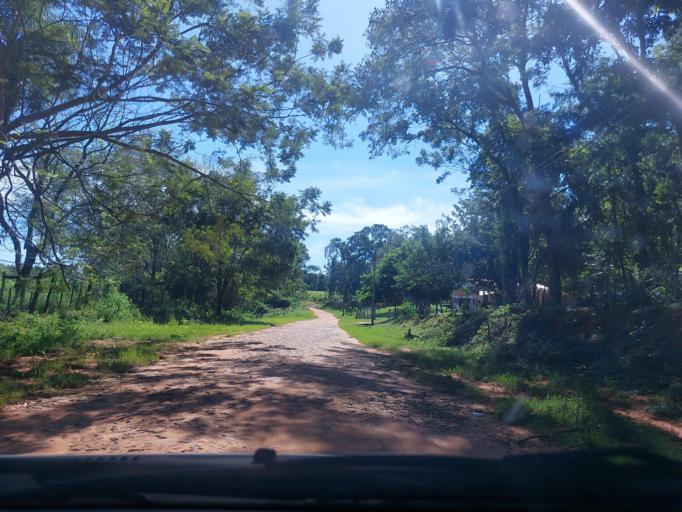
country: PY
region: San Pedro
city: Itacurubi del Rosario
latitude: -24.5559
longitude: -56.5889
